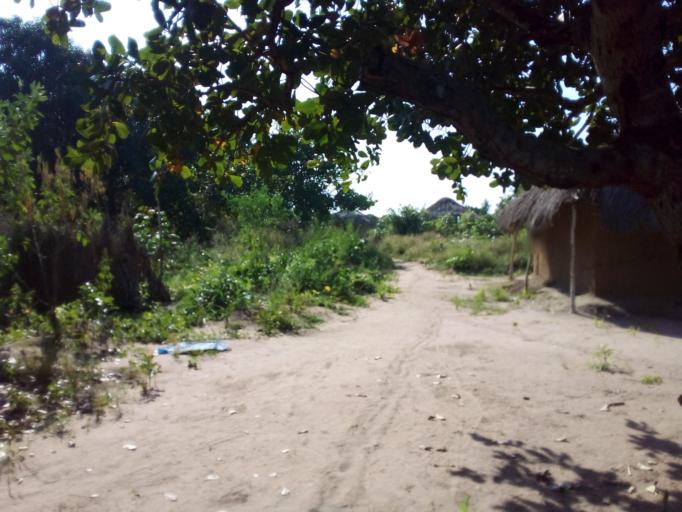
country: MZ
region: Zambezia
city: Quelimane
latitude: -17.5542
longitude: 36.7025
